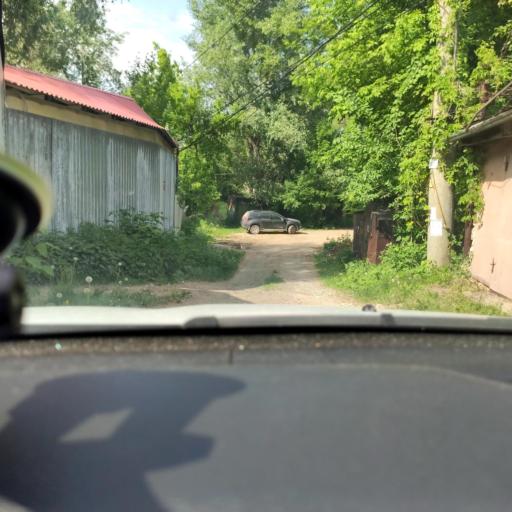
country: RU
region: Samara
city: Volzhskiy
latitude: 53.3357
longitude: 50.1960
